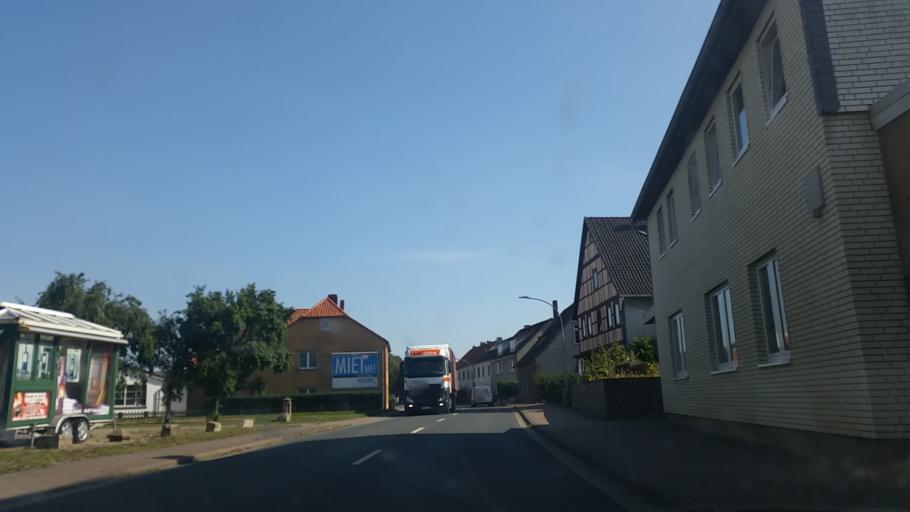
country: DE
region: Lower Saxony
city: Coppenbrugge
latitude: 52.1077
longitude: 9.5707
